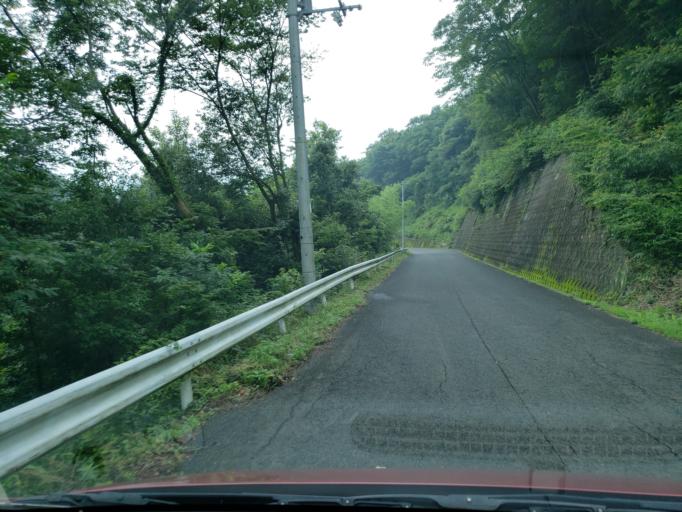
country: JP
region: Tokushima
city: Kamojimacho-jogejima
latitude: 34.1093
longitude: 134.2985
